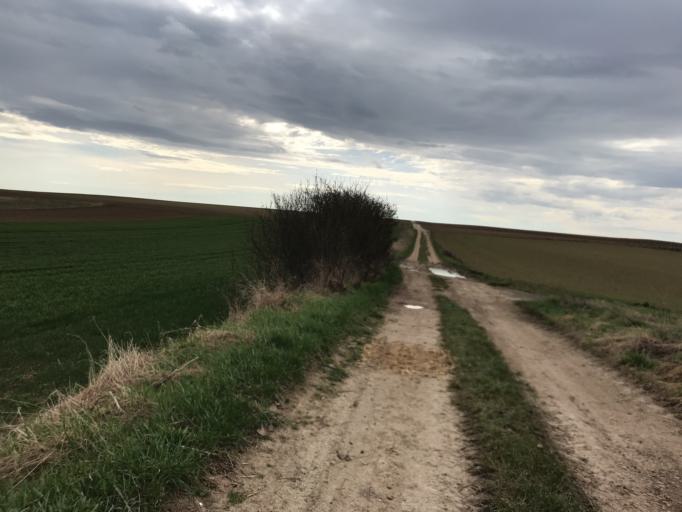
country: DE
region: Rheinland-Pfalz
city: Stadecken-Elsheim
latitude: 49.8917
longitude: 8.1386
